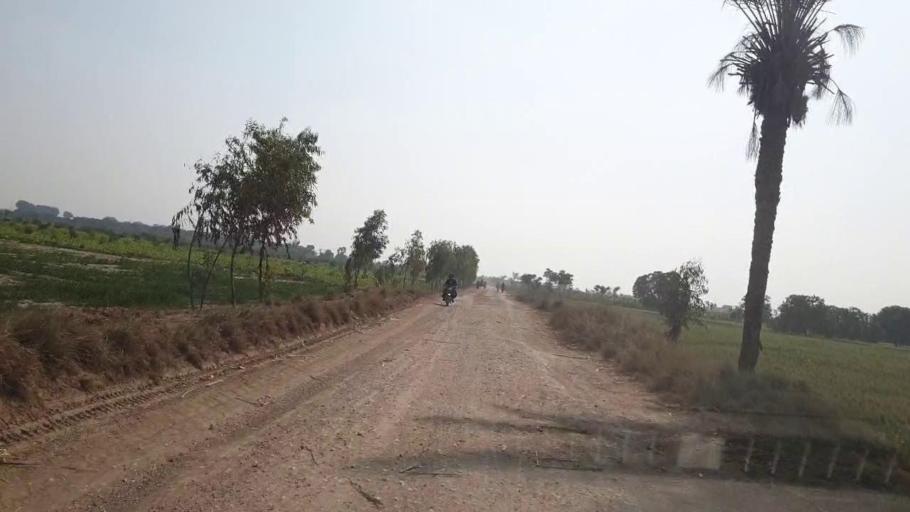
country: PK
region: Sindh
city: Bhit Shah
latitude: 25.7146
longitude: 68.5459
